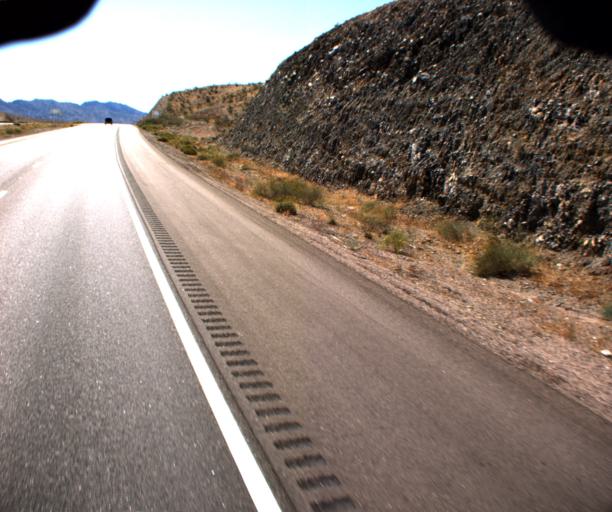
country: US
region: Nevada
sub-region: Clark County
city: Boulder City
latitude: 35.9675
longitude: -114.6748
